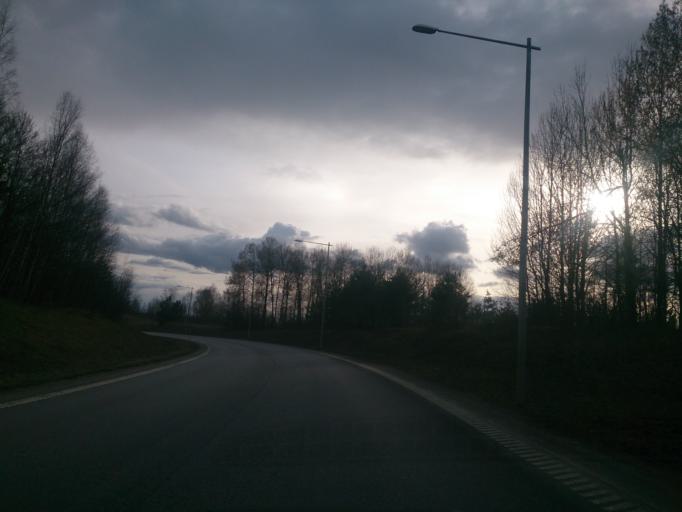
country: SE
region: OEstergoetland
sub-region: Norrkopings Kommun
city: Jursla
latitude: 58.6351
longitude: 16.1569
